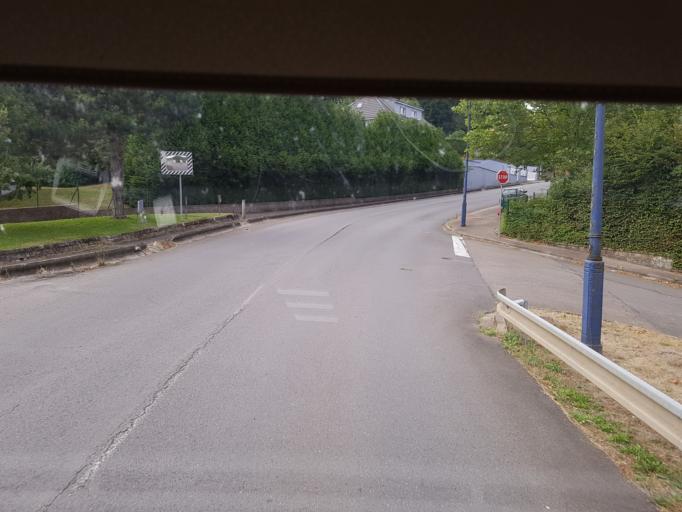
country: FR
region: Lorraine
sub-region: Departement de la Moselle
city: Moyeuvre-Grande
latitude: 49.2462
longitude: 6.0371
